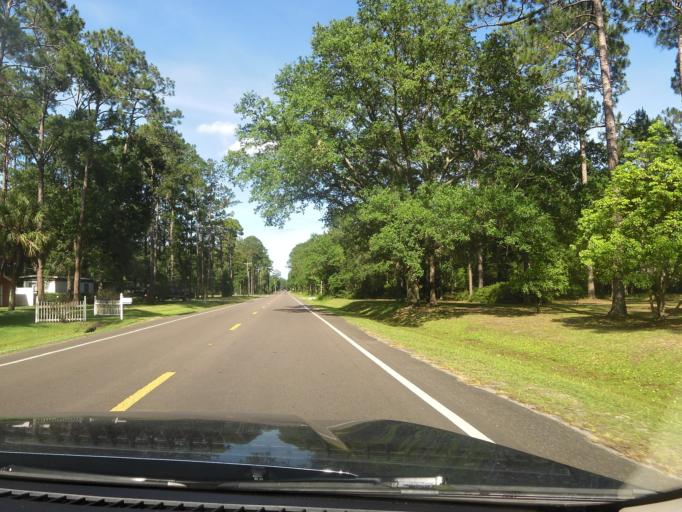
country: US
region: Florida
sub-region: Nassau County
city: Callahan
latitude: 30.5564
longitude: -81.8726
